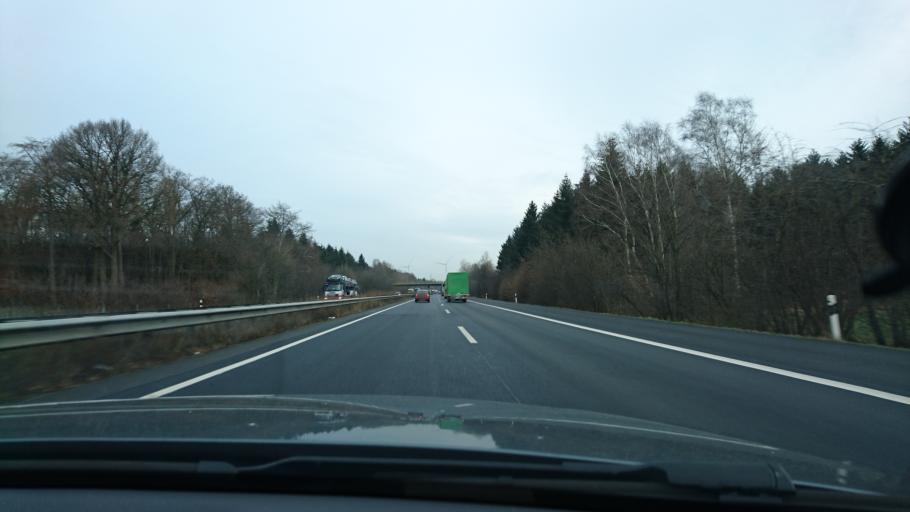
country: DE
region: Lower Saxony
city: Rieste
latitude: 52.4344
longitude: 8.0333
